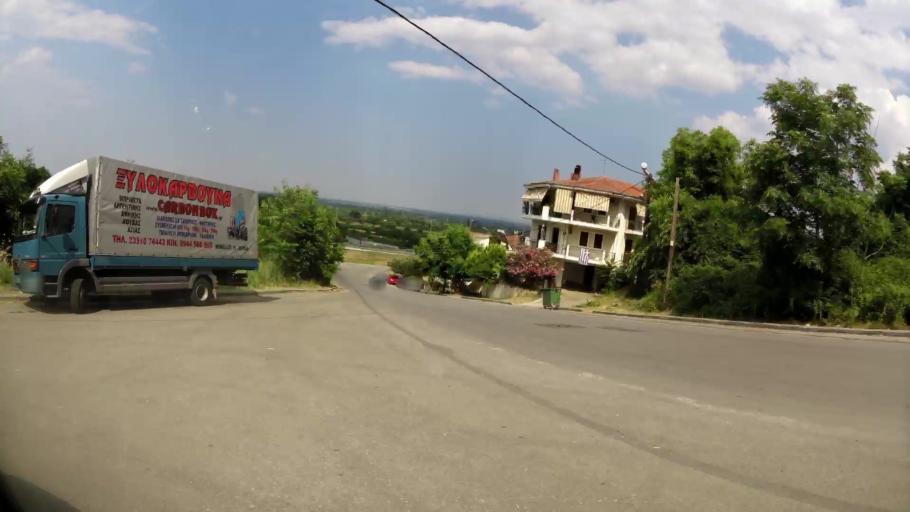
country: GR
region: Central Macedonia
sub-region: Nomos Imathias
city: Veroia
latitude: 40.5136
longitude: 22.2105
